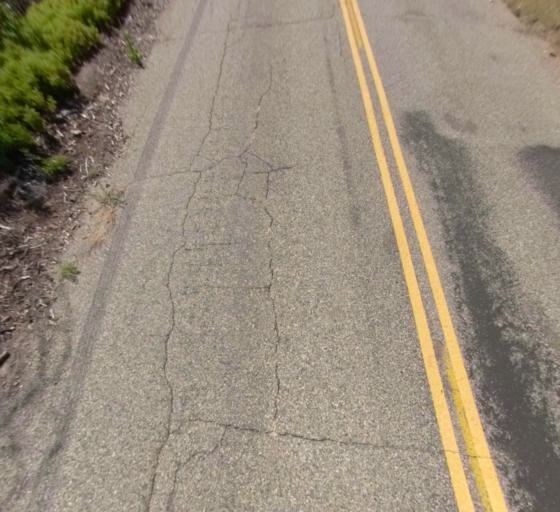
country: US
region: California
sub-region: Fresno County
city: Auberry
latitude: 37.3008
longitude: -119.3509
